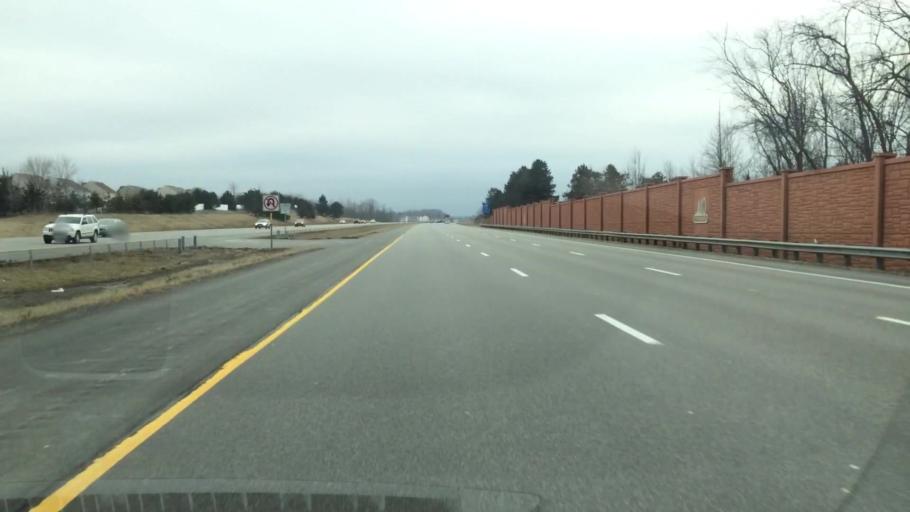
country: US
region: Ohio
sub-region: Cuyahoga County
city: Strongsville
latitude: 41.2748
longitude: -81.8063
